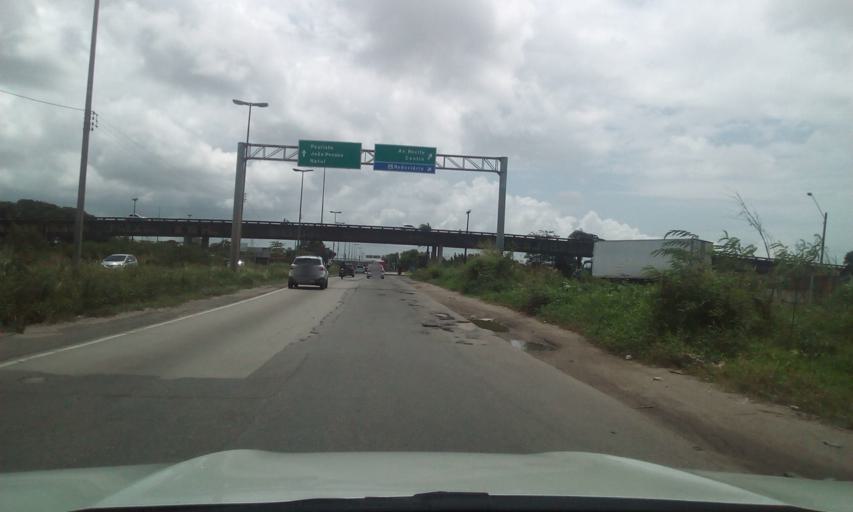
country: BR
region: Pernambuco
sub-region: Recife
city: Recife
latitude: -8.0765
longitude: -34.9428
